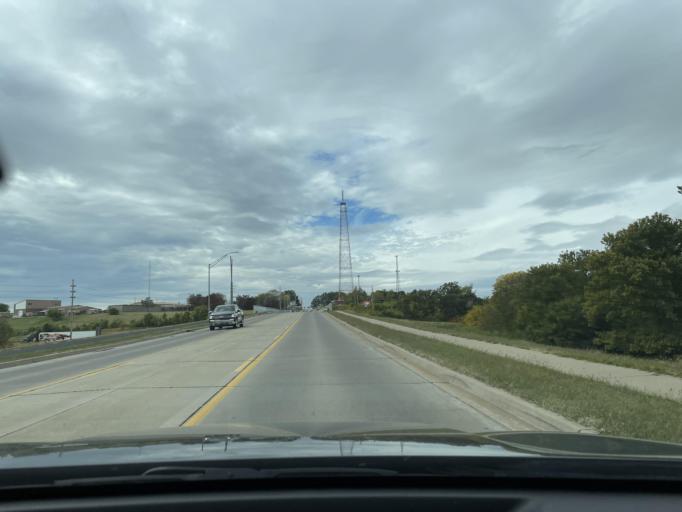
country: US
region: Missouri
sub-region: Buchanan County
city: Saint Joseph
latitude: 39.7698
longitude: -94.7907
